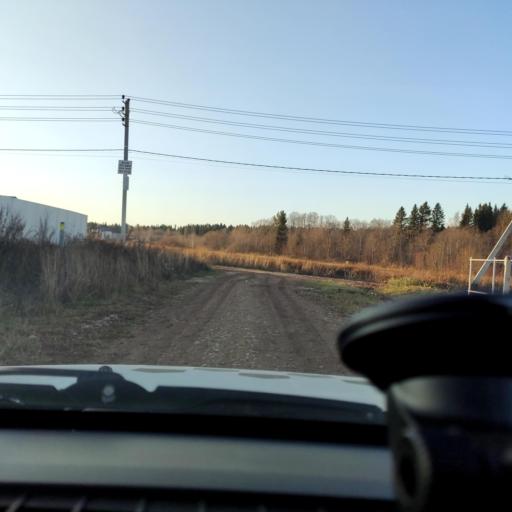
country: RU
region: Perm
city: Ferma
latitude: 57.9483
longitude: 56.3472
